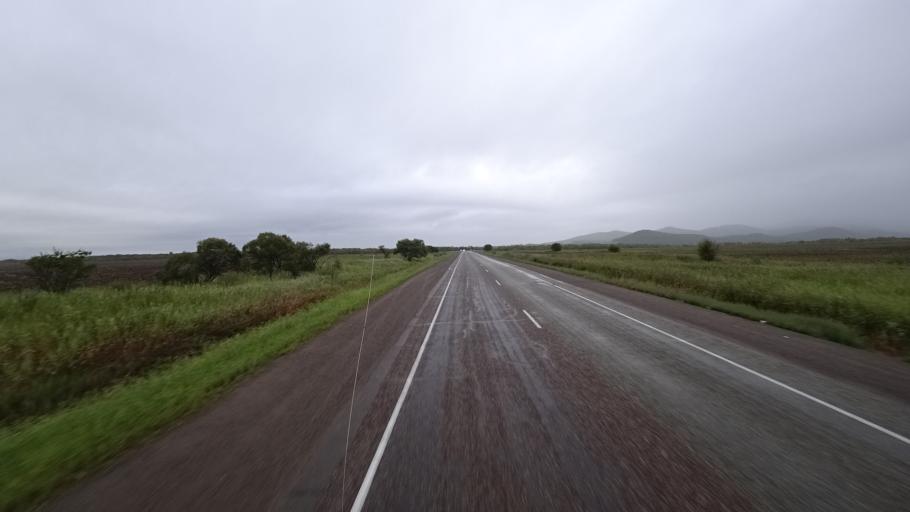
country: RU
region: Primorskiy
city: Monastyrishche
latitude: 44.2845
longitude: 132.4974
